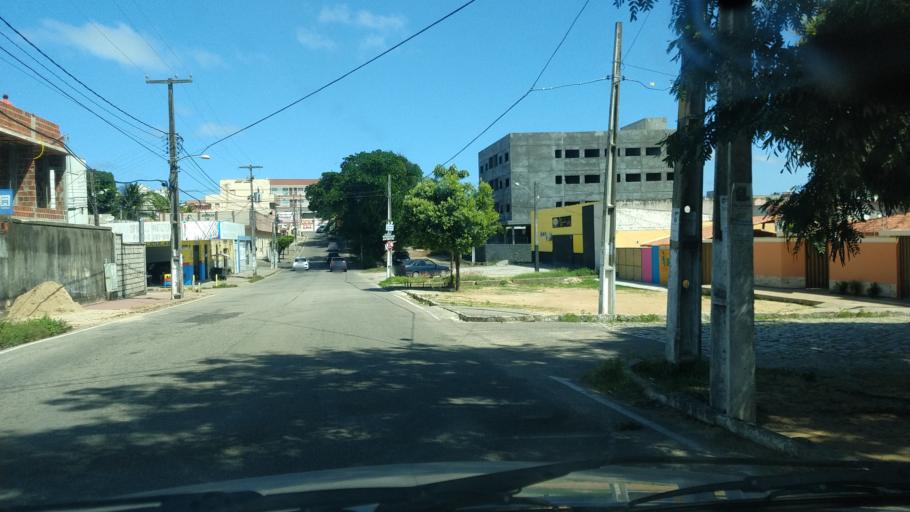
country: BR
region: Rio Grande do Norte
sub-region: Natal
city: Natal
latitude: -5.8590
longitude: -35.2072
